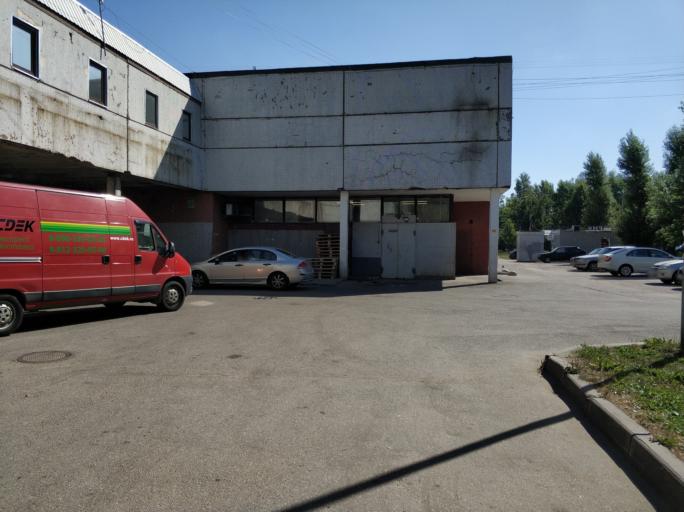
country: RU
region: Leningrad
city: Akademicheskoe
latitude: 60.0159
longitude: 30.3984
